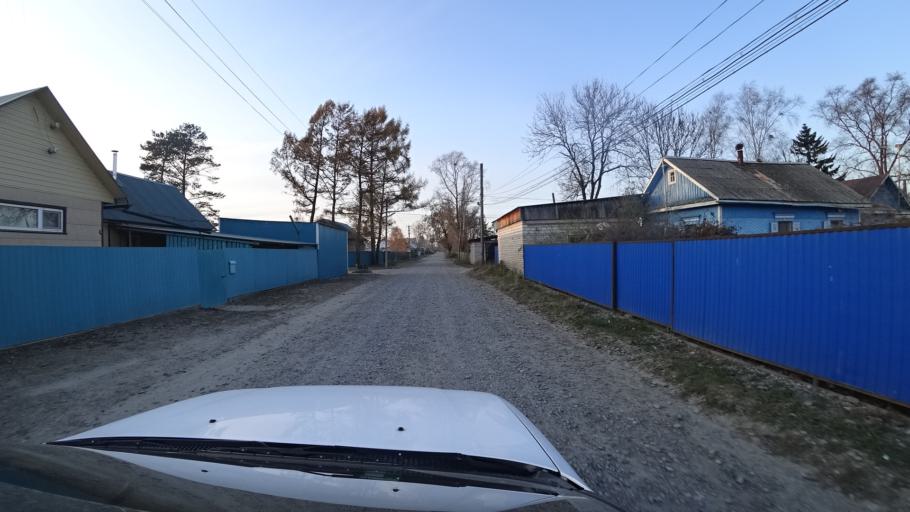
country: RU
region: Primorskiy
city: Dal'nerechensk
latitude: 45.9457
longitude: 133.8220
